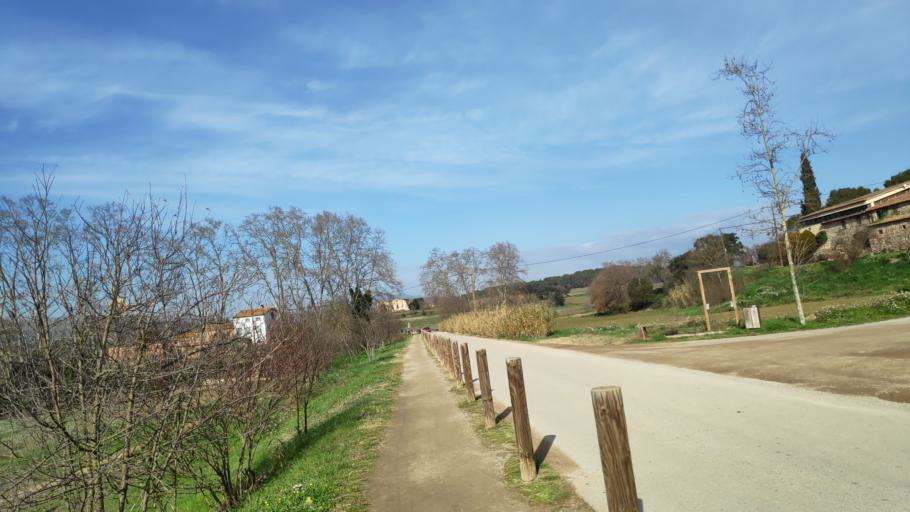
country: ES
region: Catalonia
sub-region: Provincia de Barcelona
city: Mollet del Valles
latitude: 41.5593
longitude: 2.2018
